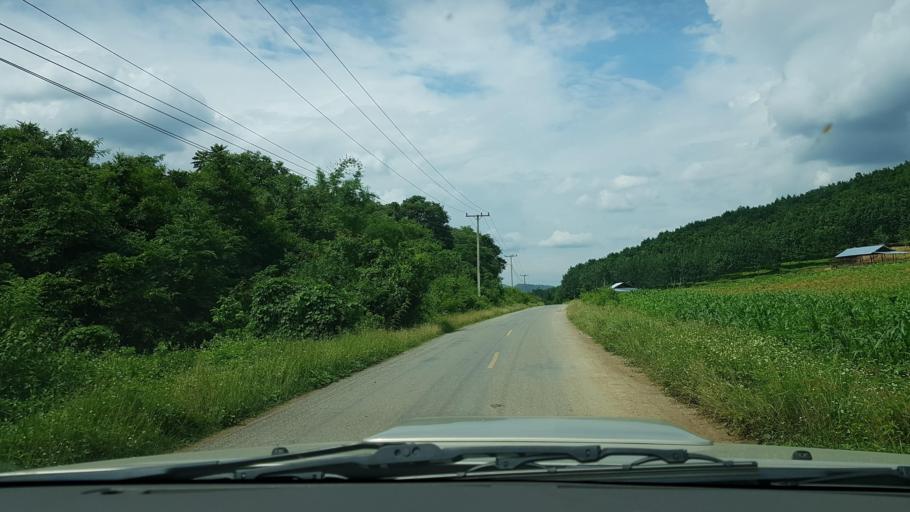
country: LA
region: Loungnamtha
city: Muang Nale
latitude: 20.2602
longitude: 101.5922
